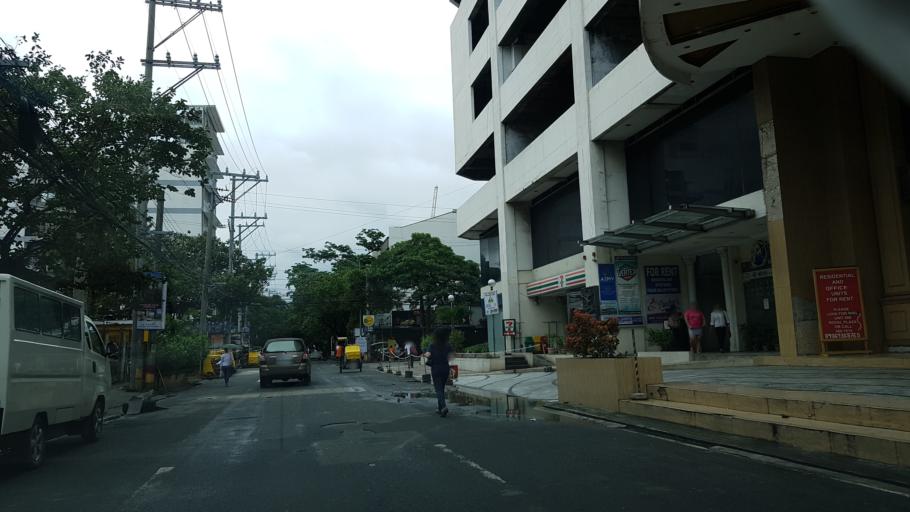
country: PH
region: Metro Manila
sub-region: City of Manila
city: Port Area
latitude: 14.5711
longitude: 120.9878
